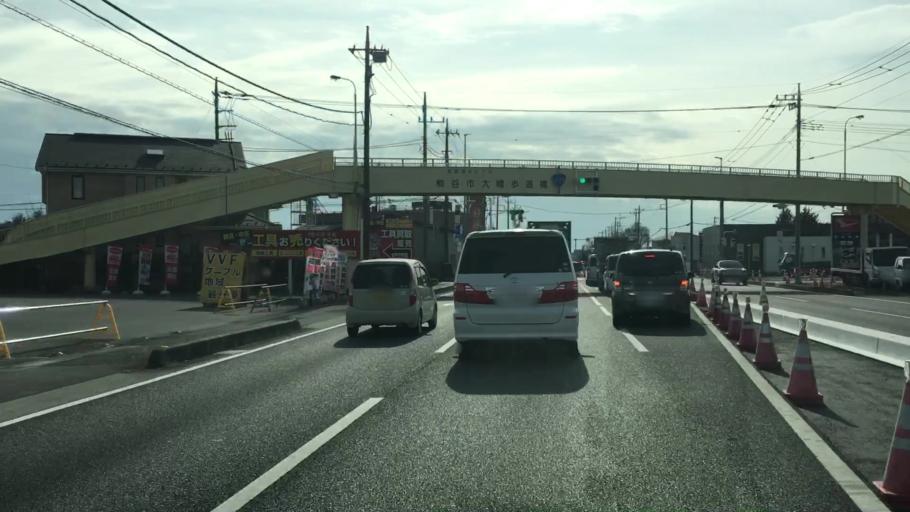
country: JP
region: Saitama
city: Kumagaya
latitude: 36.1700
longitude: 139.3705
